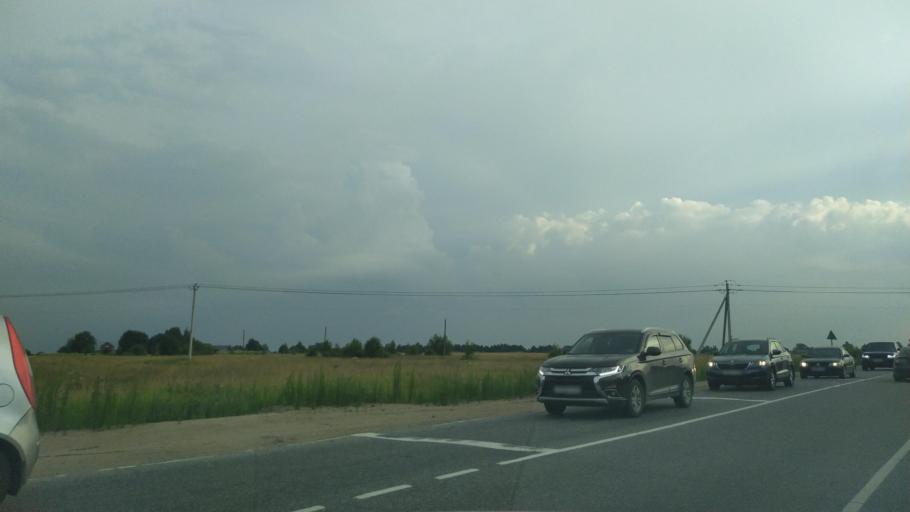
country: RU
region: Leningrad
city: Koltushi
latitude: 59.8903
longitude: 30.7333
